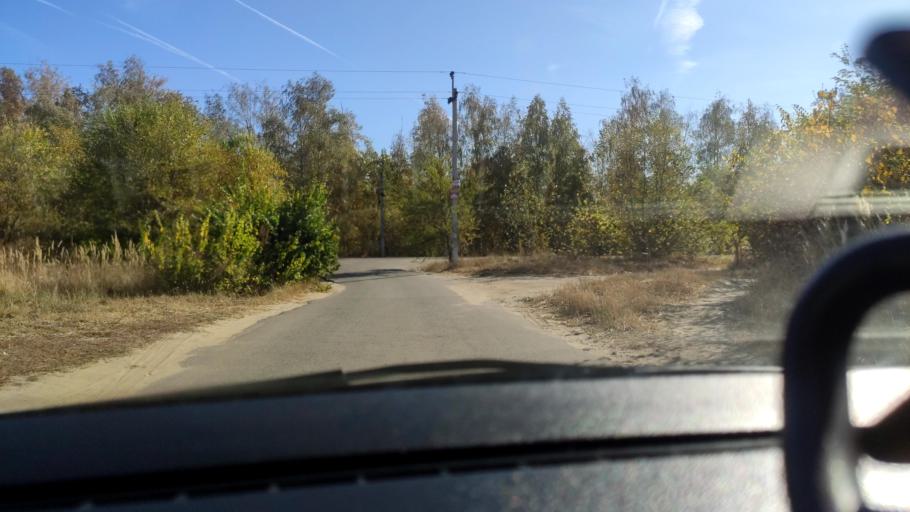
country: RU
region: Voronezj
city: Pridonskoy
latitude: 51.6392
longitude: 39.0883
